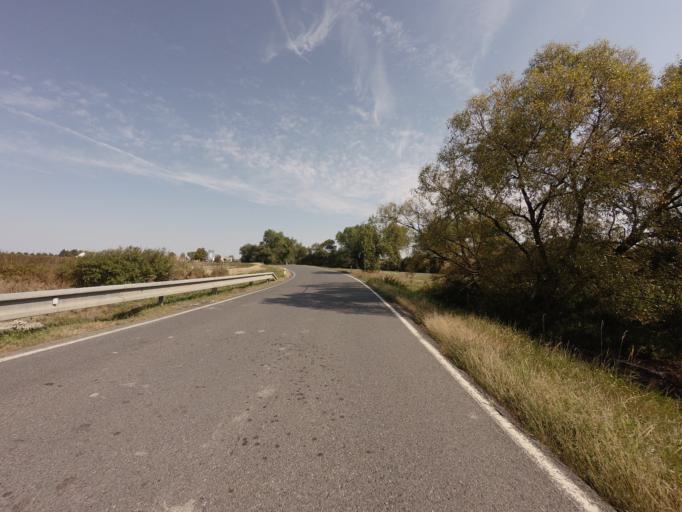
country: CZ
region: Jihocesky
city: Bernartice
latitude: 49.3594
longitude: 14.3773
